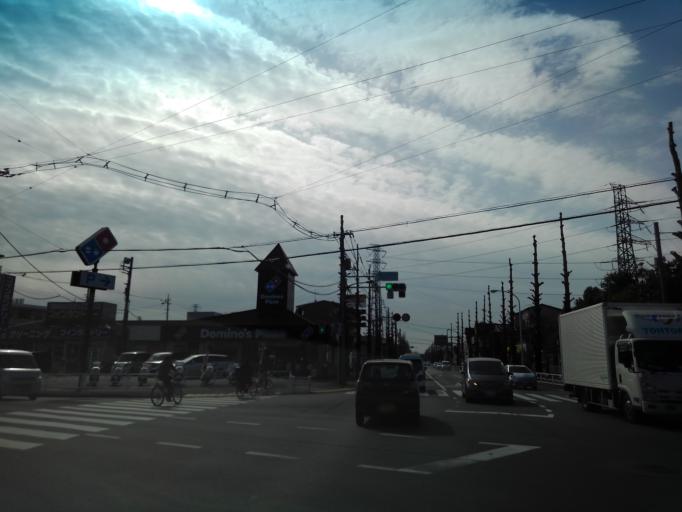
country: JP
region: Tokyo
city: Tanashicho
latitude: 35.7517
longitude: 139.5058
